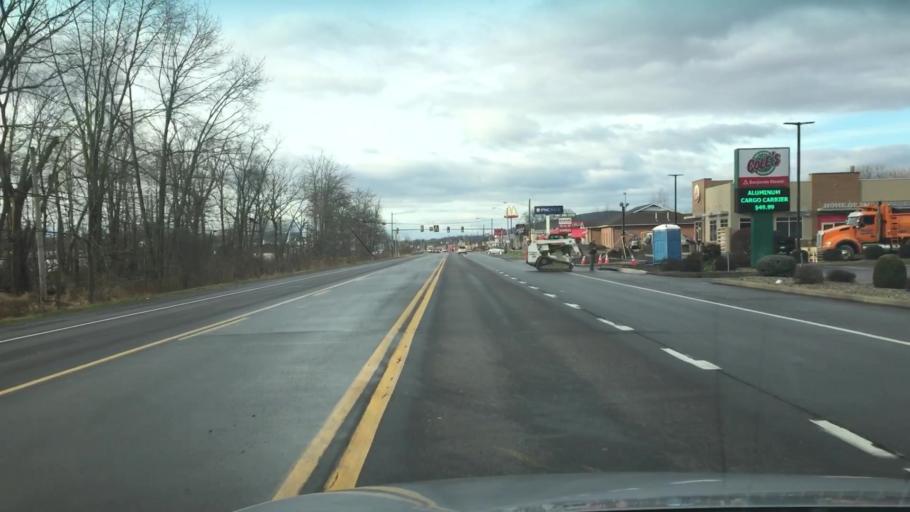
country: US
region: Pennsylvania
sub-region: Columbia County
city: Bloomsburg
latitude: 41.0056
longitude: -76.4334
